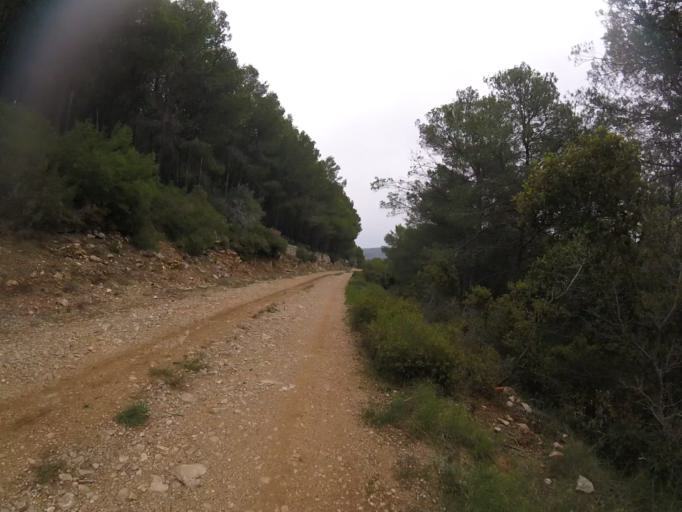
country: ES
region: Valencia
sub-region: Provincia de Castello
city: Alcala de Xivert
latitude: 40.3102
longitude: 0.2619
